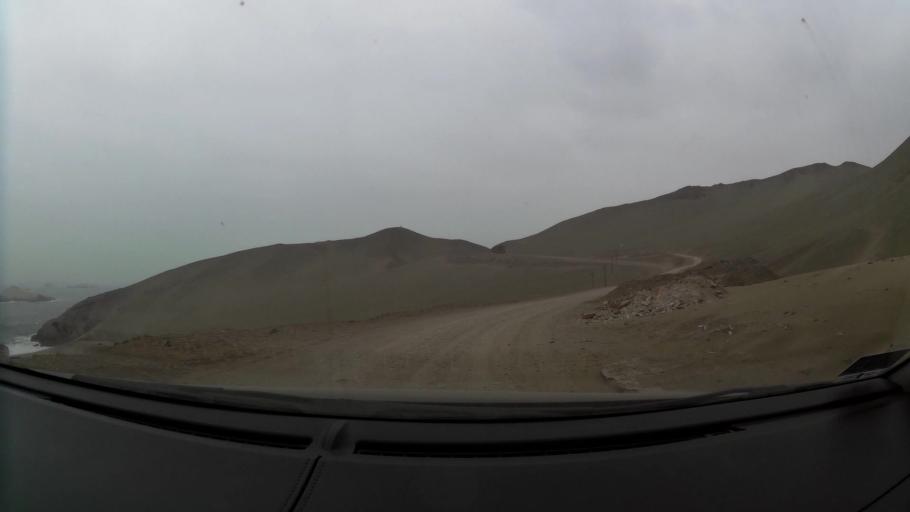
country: PE
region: Lima
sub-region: Lima
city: Santa Rosa
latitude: -11.8114
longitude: -77.1732
